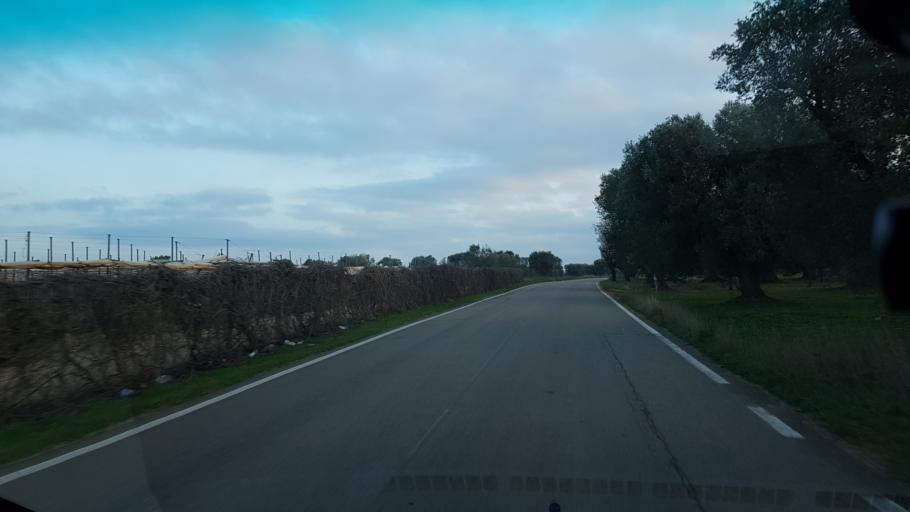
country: IT
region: Apulia
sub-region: Provincia di Brindisi
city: Mesagne
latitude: 40.6265
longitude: 17.7837
